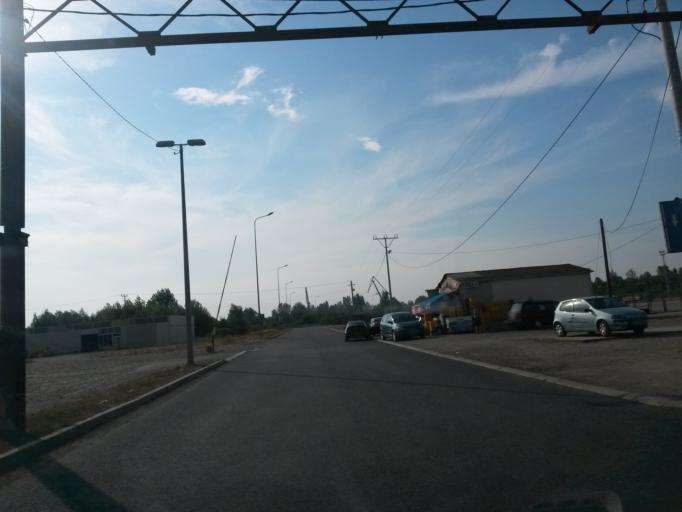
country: HR
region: Brodsko-Posavska
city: Krusevica
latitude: 45.0555
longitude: 18.4910
